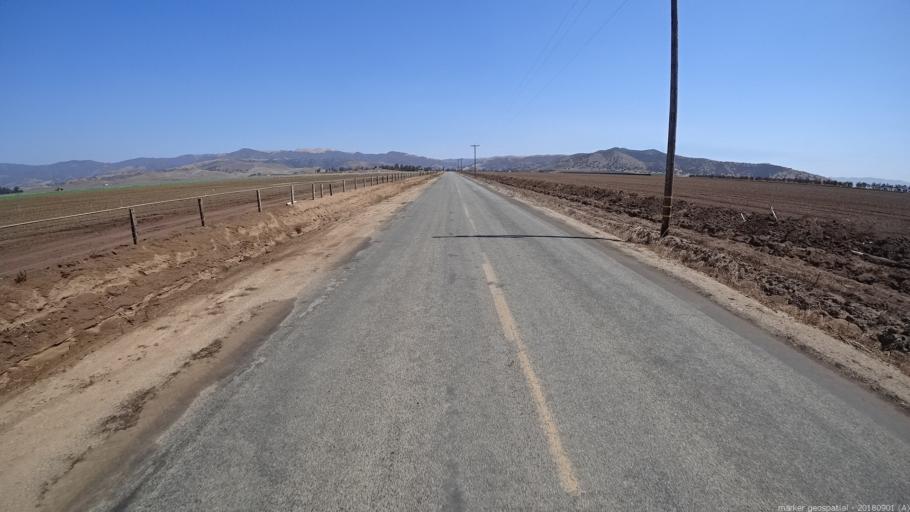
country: US
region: California
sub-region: Monterey County
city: Chualar
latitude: 36.5827
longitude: -121.4776
